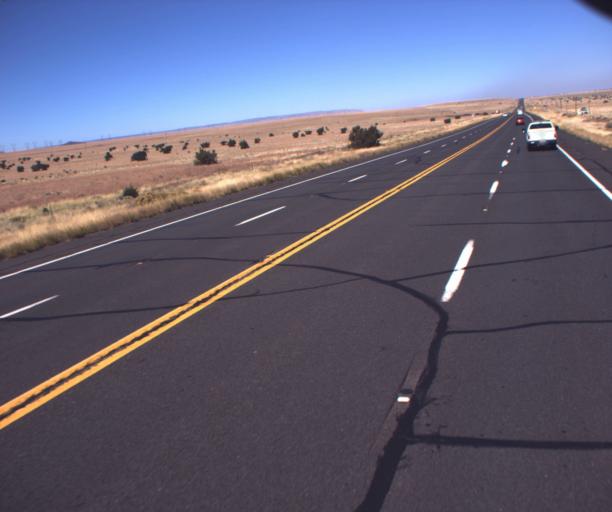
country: US
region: Arizona
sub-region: Coconino County
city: Flagstaff
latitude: 35.5465
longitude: -111.5377
